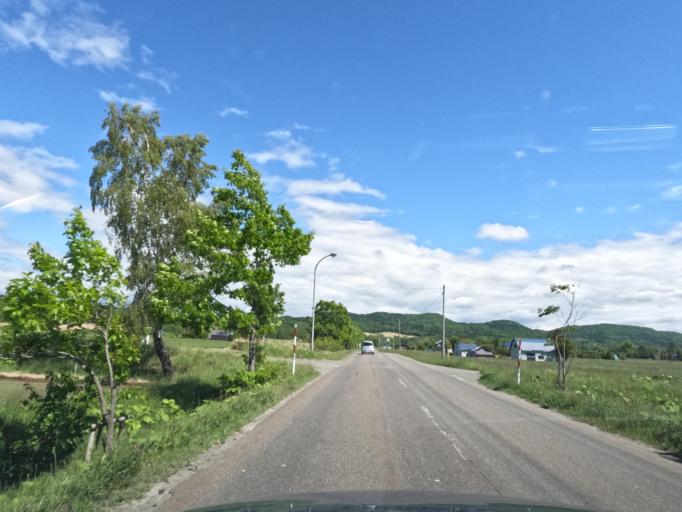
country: JP
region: Hokkaido
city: Kitahiroshima
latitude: 43.0172
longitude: 141.7202
